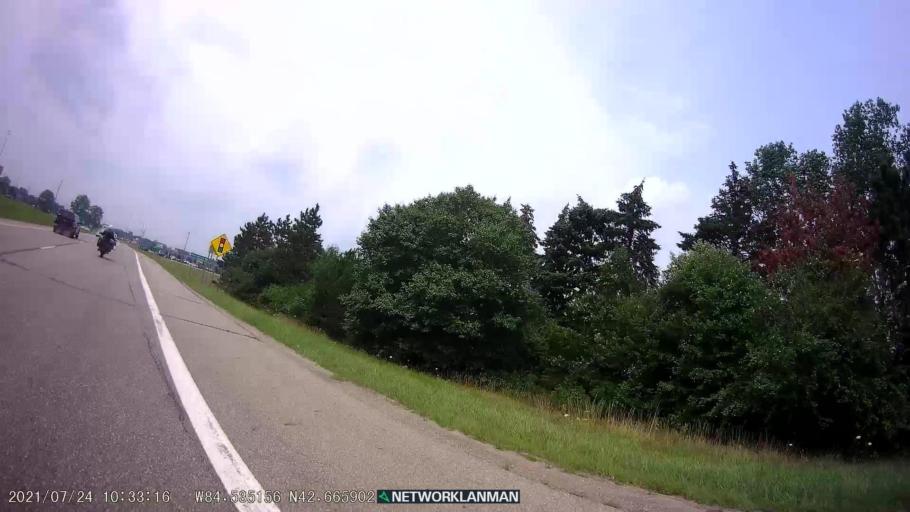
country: US
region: Michigan
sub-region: Ingham County
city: Holt
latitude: 42.6663
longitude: -84.5360
